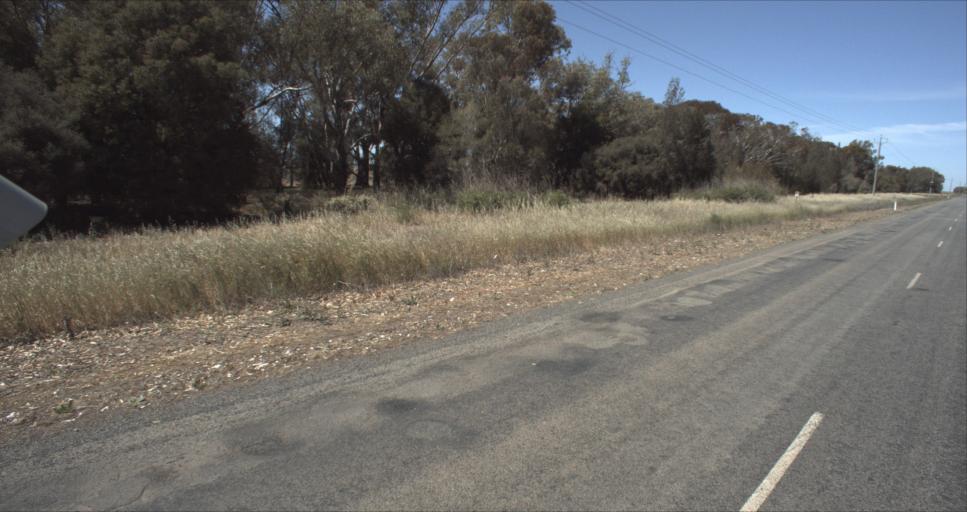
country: AU
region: New South Wales
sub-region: Leeton
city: Leeton
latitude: -34.4664
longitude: 146.2932
